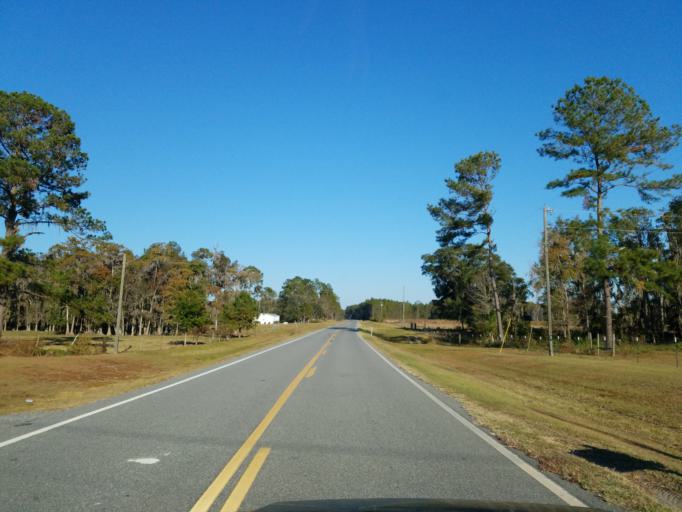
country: US
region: Georgia
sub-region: Echols County
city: Statenville
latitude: 30.6305
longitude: -83.0824
